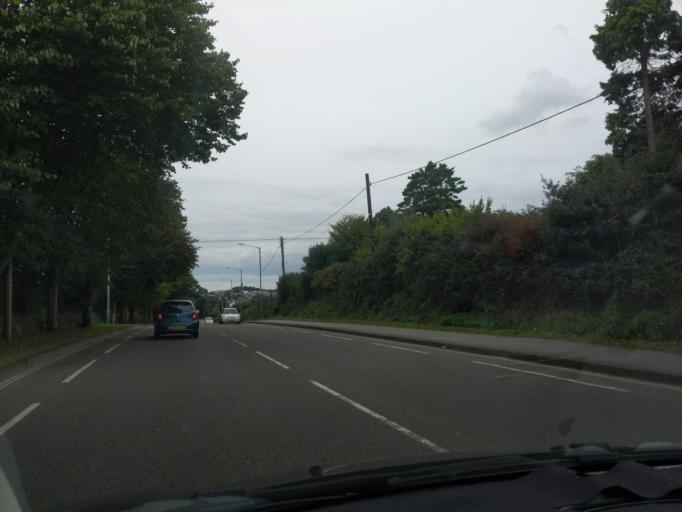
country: GB
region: England
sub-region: Cornwall
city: St Austell
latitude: 50.3340
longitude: -4.7805
